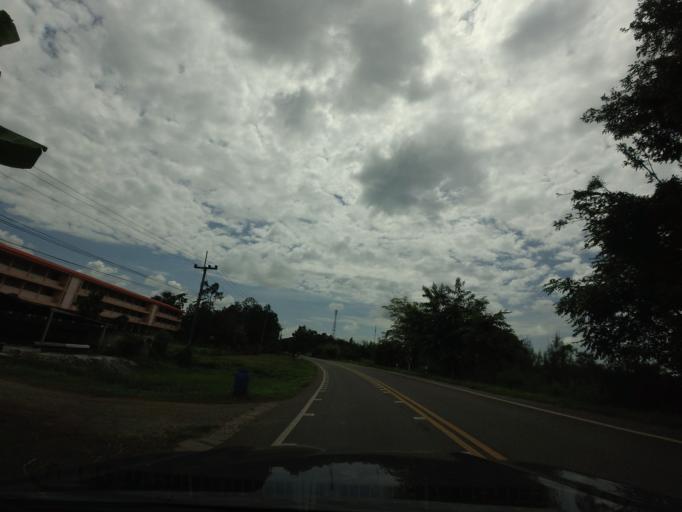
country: TH
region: Changwat Udon Thani
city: Nam Som
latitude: 17.8058
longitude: 102.2732
